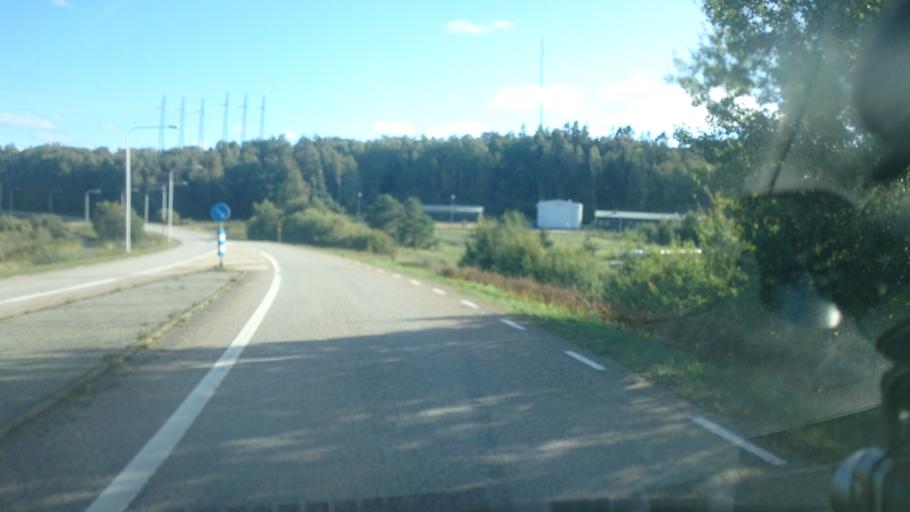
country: SE
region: Vaestra Goetaland
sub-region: Lysekils Kommun
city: Lysekil
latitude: 58.3368
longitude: 11.4215
